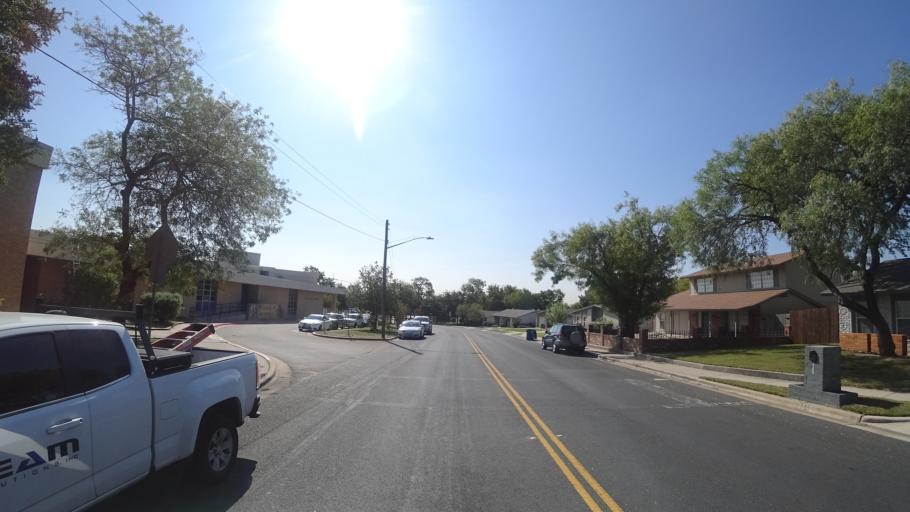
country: US
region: Texas
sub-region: Travis County
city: Austin
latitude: 30.3141
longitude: -97.6658
